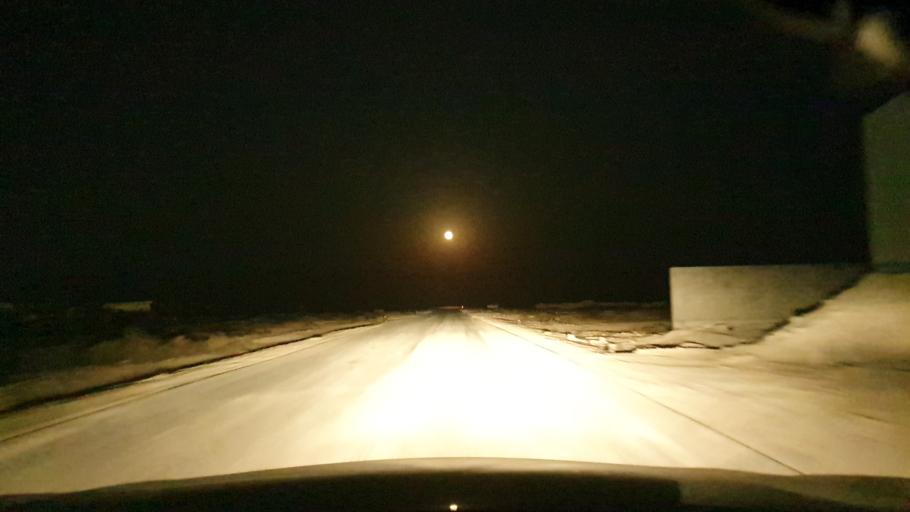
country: BH
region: Northern
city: Sitrah
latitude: 26.0973
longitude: 50.6262
